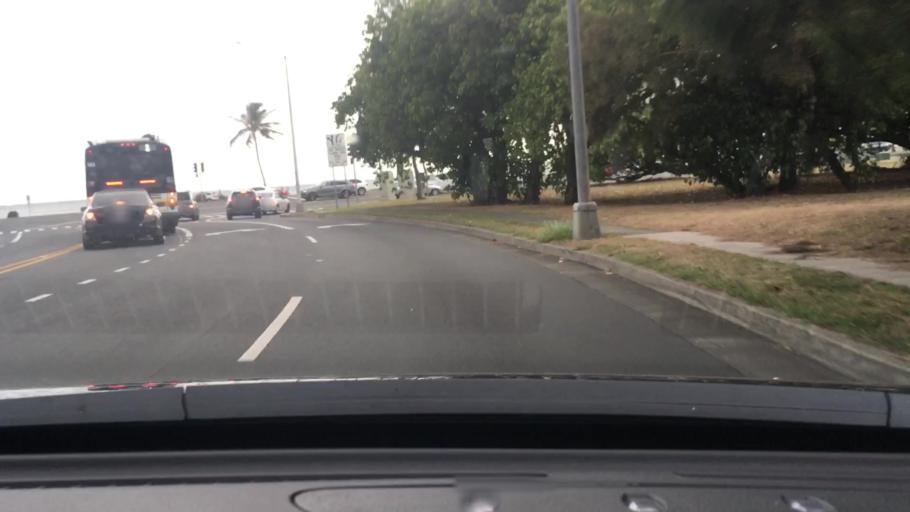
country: US
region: Hawaii
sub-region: Honolulu County
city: Waimanalo Beach
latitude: 21.2837
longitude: -157.7149
